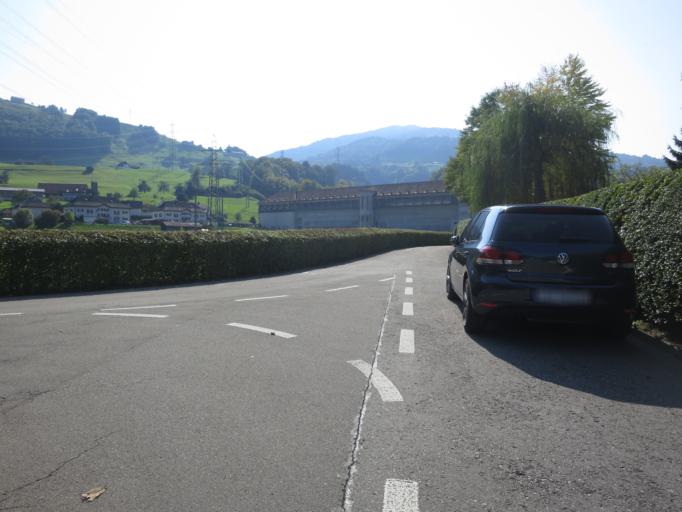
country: CH
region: Schwyz
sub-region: Bezirk March
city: Schubelbach
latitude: 47.1732
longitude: 8.9026
